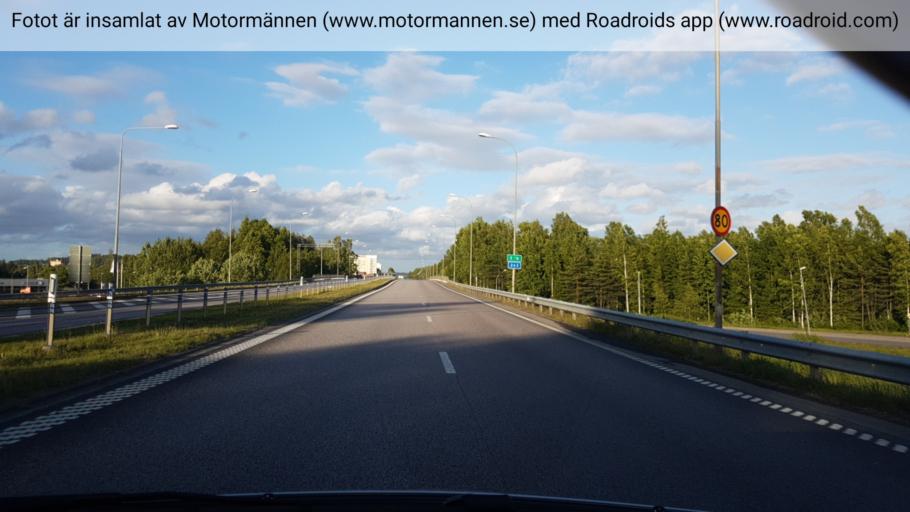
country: SE
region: OErebro
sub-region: Karlskoga Kommun
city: Karlskoga
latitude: 59.3233
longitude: 14.4770
